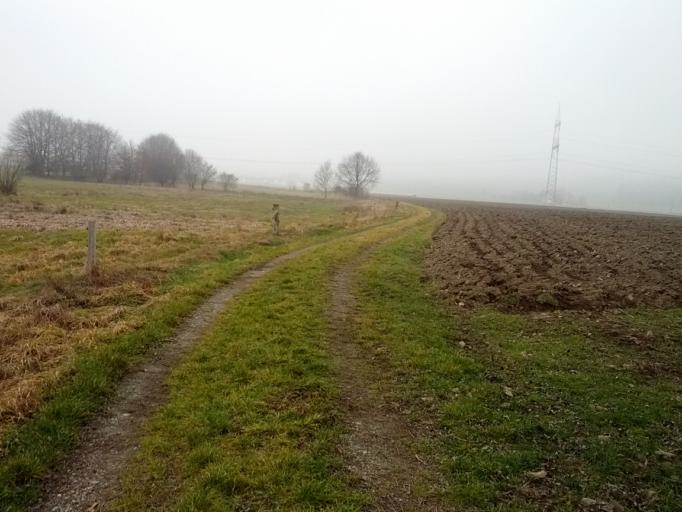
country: DE
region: Baden-Wuerttemberg
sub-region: Tuebingen Region
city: Bad Wurzach
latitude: 47.9067
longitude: 9.8507
